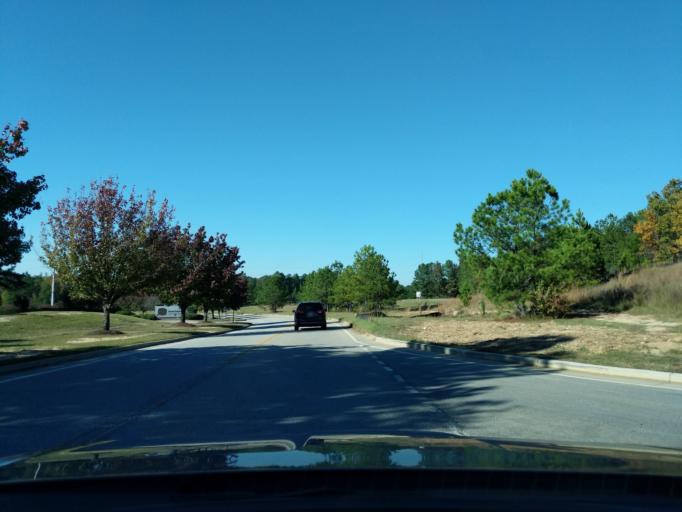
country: US
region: Georgia
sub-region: Columbia County
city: Grovetown
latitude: 33.4643
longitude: -82.1831
